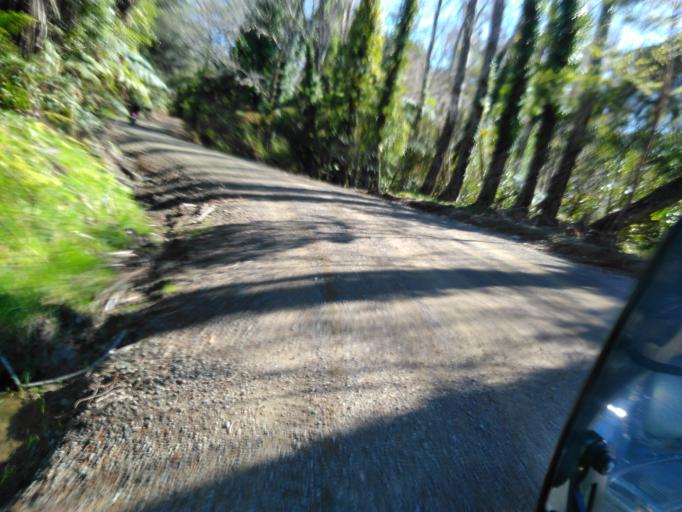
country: NZ
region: Bay of Plenty
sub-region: Opotiki District
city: Opotiki
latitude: -38.3704
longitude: 177.6009
